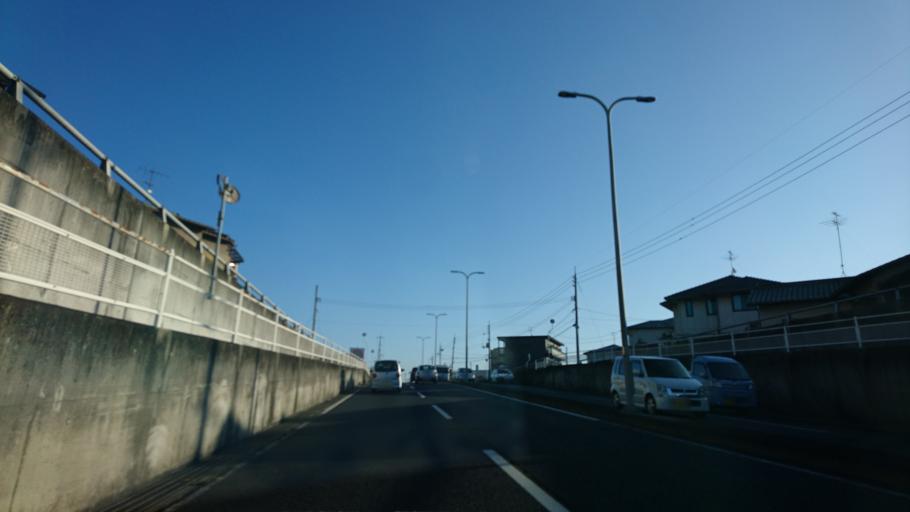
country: JP
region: Okayama
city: Kurashiki
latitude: 34.6070
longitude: 133.7573
